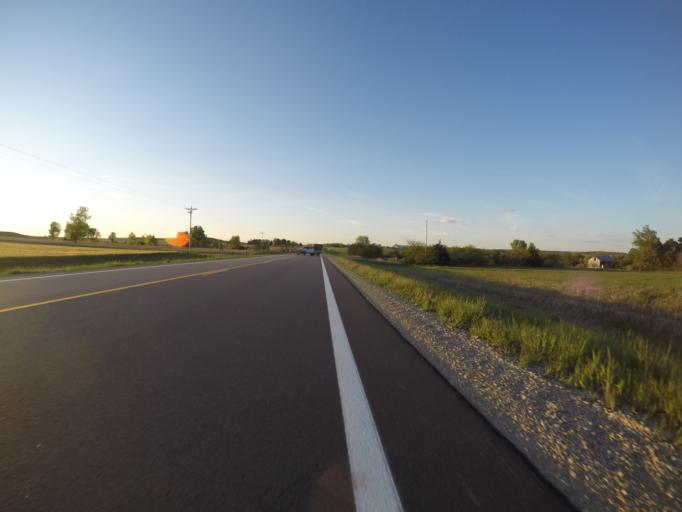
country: US
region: Kansas
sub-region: Pottawatomie County
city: Westmoreland
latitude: 39.3916
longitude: -96.5199
